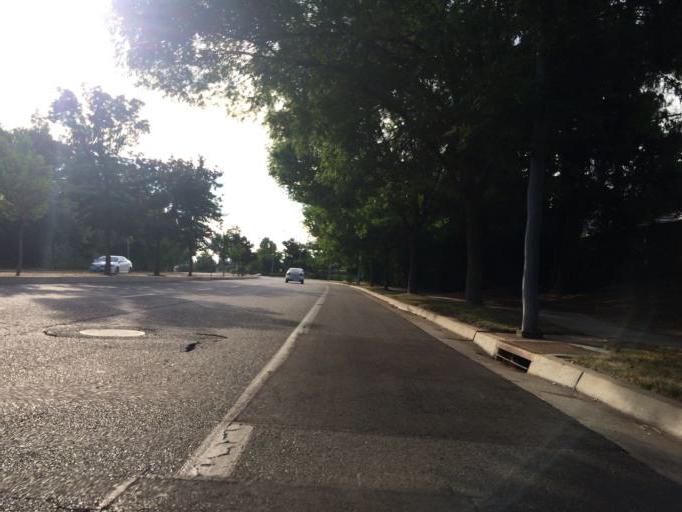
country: US
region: California
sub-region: Fresno County
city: Clovis
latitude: 36.8701
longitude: -119.7601
